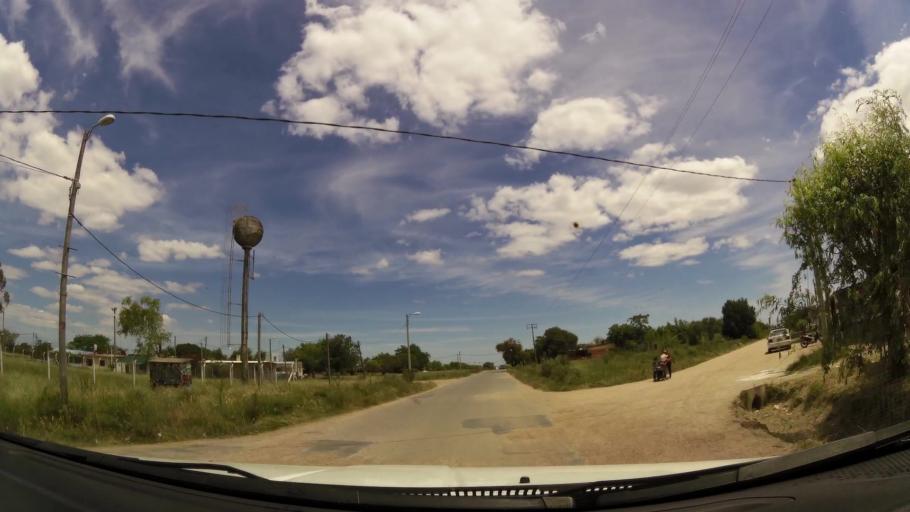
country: UY
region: San Jose
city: Delta del Tigre
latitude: -34.7514
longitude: -56.4206
